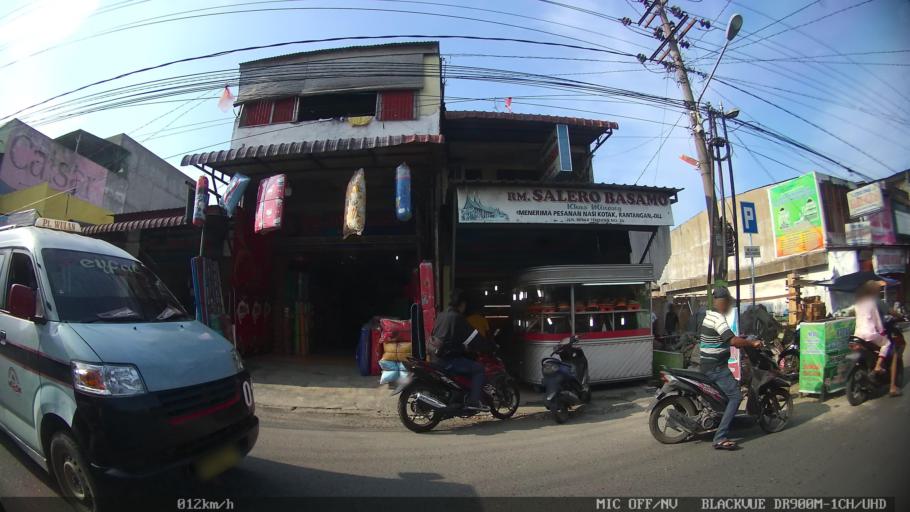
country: ID
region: North Sumatra
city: Medan
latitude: 3.5970
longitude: 98.7469
